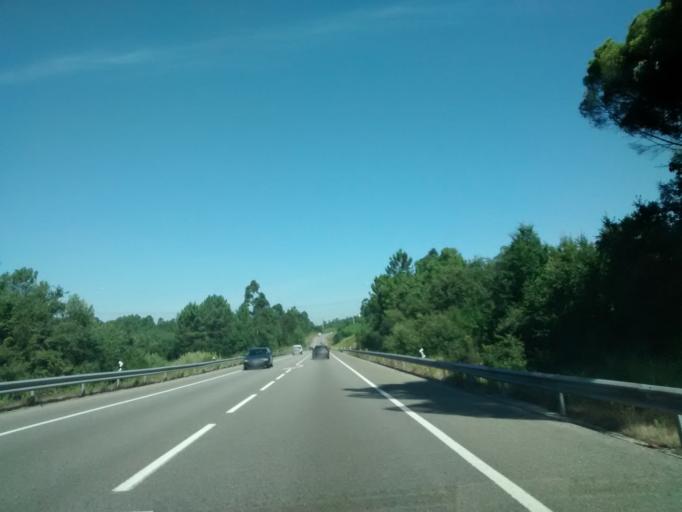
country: PT
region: Aveiro
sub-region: Oliveira do Bairro
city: Oliveira do Bairro
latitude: 40.5002
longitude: -8.4867
